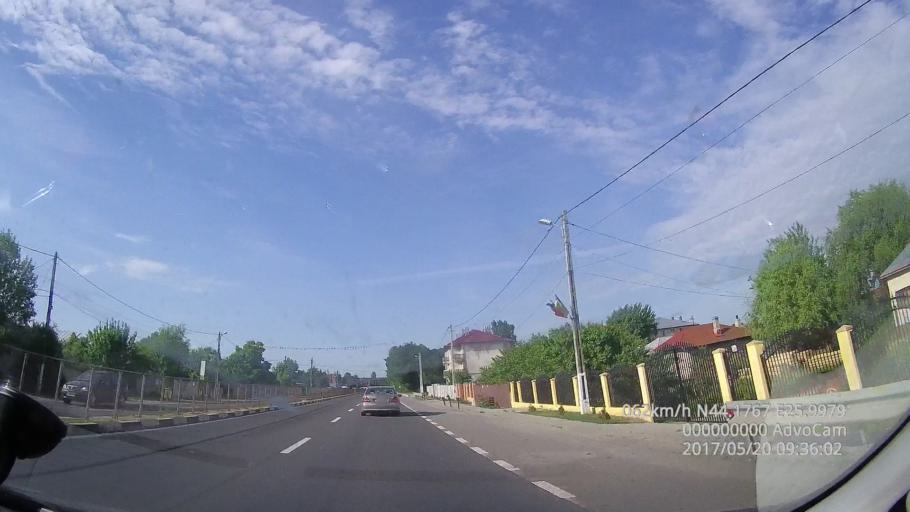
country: RO
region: Giurgiu
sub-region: Comuna Calugareni
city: Calugareni
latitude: 44.1766
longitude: 25.9978
